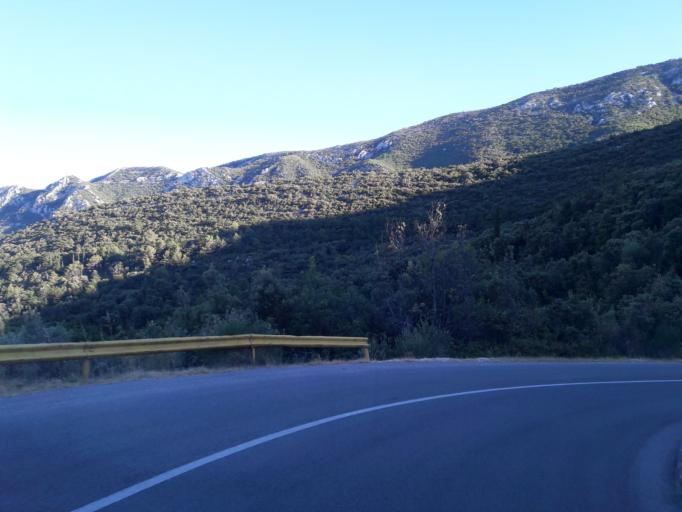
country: HR
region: Dubrovacko-Neretvanska
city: Orebic
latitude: 42.9967
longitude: 17.2637
